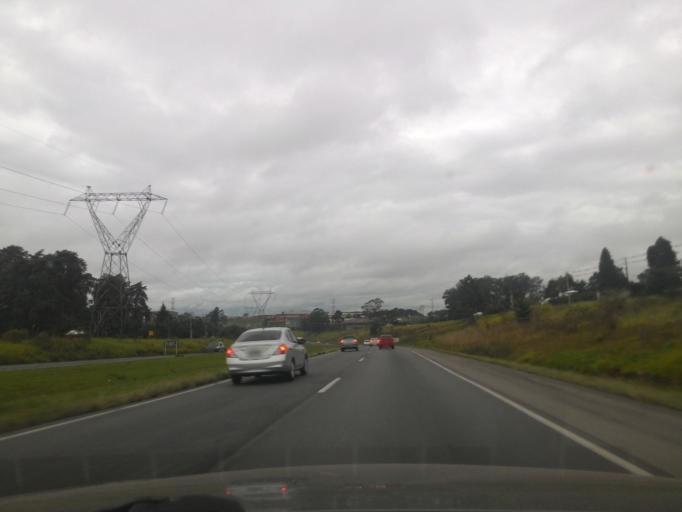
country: BR
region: Parana
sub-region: Araucaria
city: Araucaria
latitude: -25.5475
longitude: -49.3202
